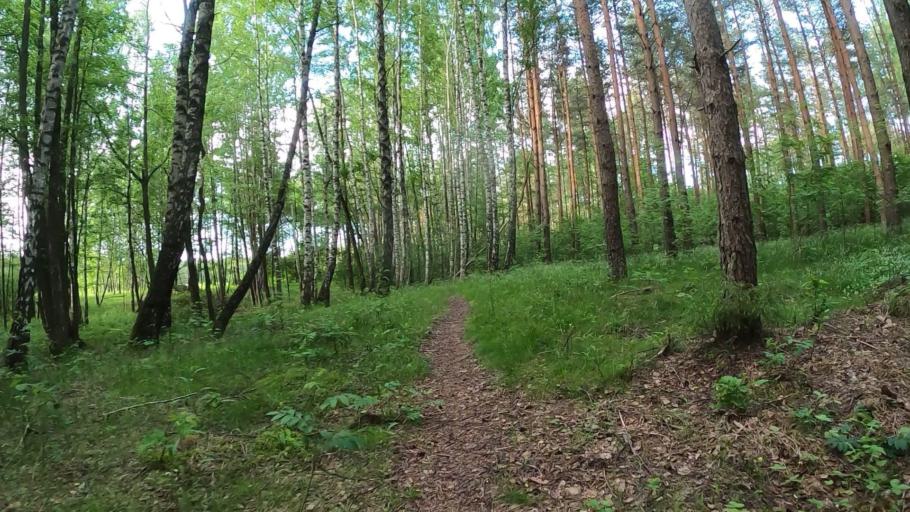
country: LV
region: Riga
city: Jaunciems
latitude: 57.0633
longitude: 24.1322
